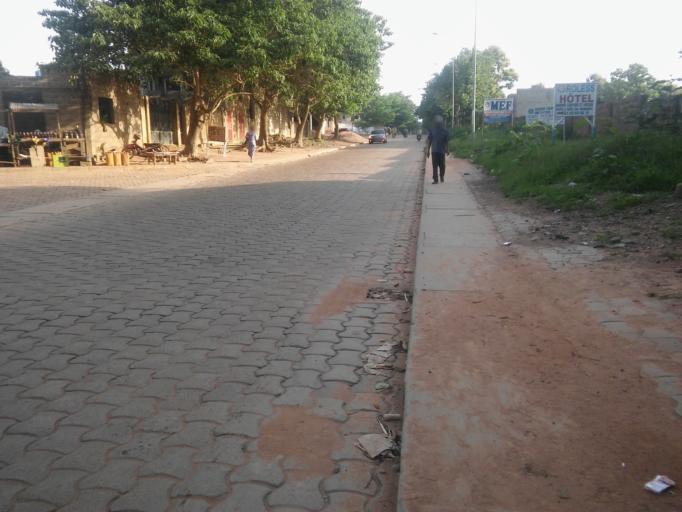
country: BJ
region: Borgou
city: Parakou
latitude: 9.3606
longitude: 2.6347
